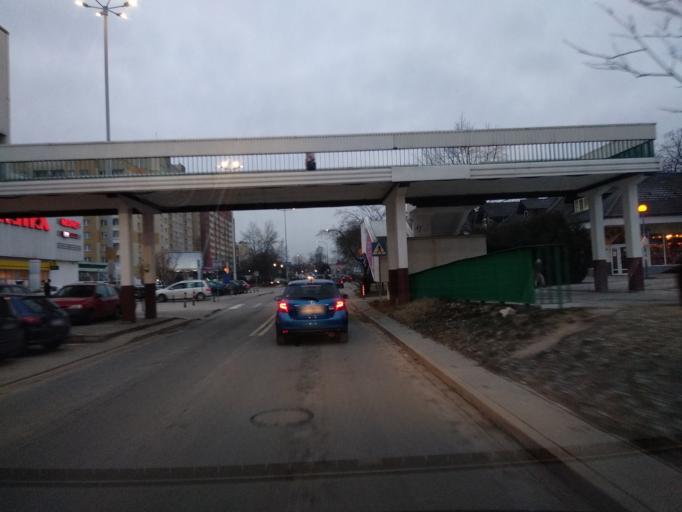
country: PL
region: Lower Silesian Voivodeship
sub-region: Powiat wroclawski
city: Wroclaw
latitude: 51.1271
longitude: 16.9764
